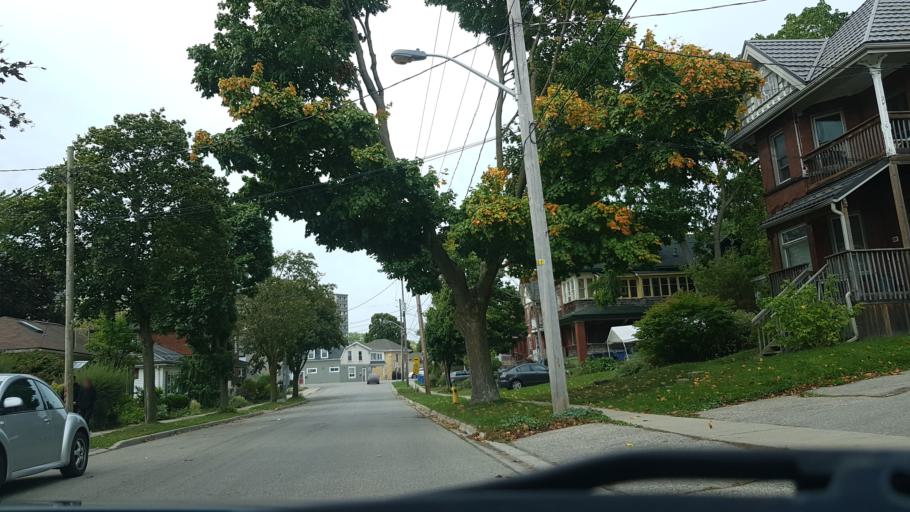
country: CA
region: Ontario
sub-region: Wellington County
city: Guelph
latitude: 43.5494
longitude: -80.2490
